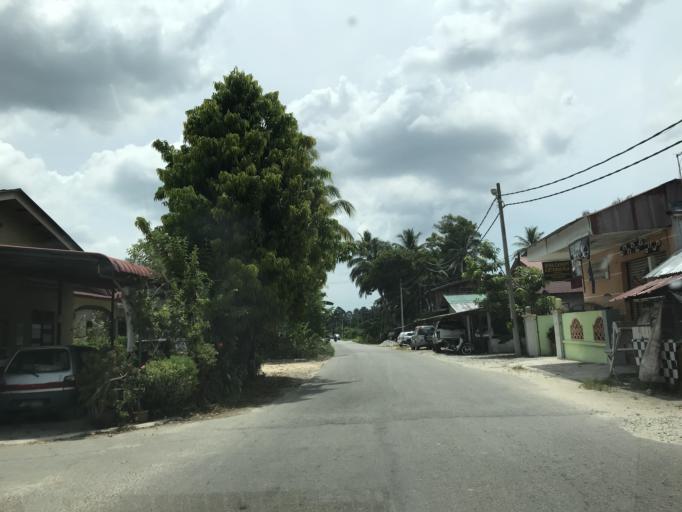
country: MY
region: Kelantan
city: Kota Bharu
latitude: 6.1463
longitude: 102.1872
